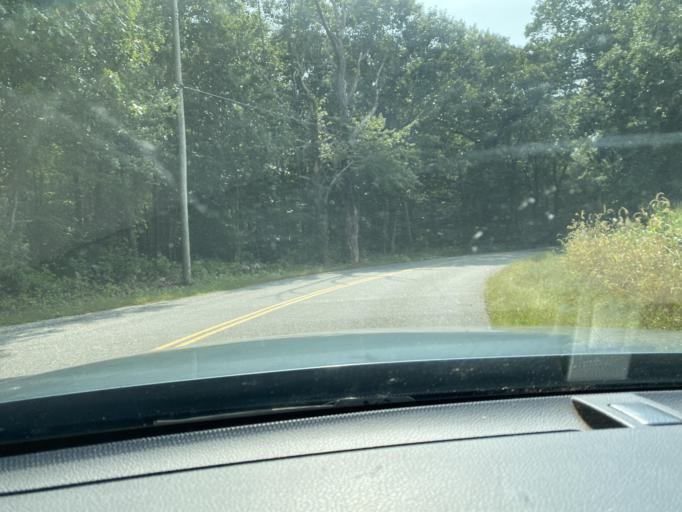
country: US
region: Connecticut
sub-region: New London County
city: Colchester
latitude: 41.6163
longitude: -72.3093
